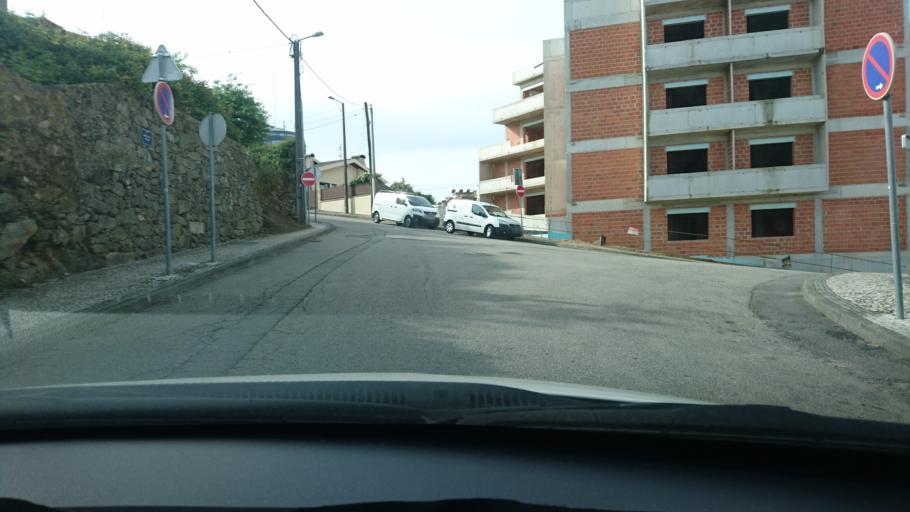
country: PT
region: Aveiro
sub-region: Oliveira de Azemeis
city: Oliveira de Azemeis
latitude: 40.8413
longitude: -8.4808
